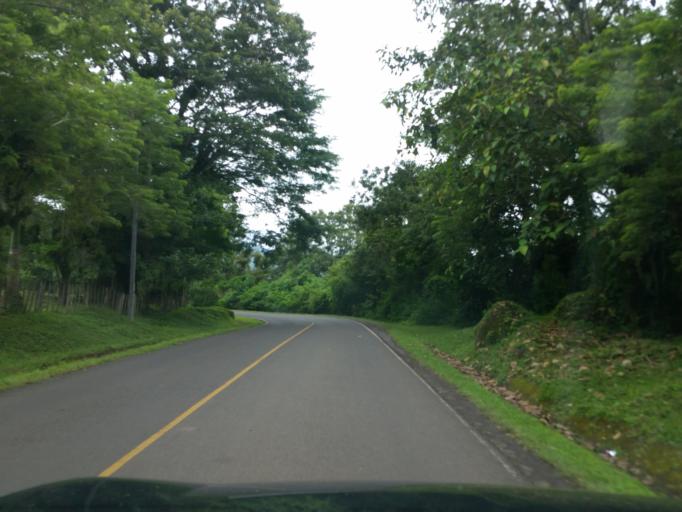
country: NI
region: Matagalpa
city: San Ramon
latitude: 12.9786
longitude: -85.8473
